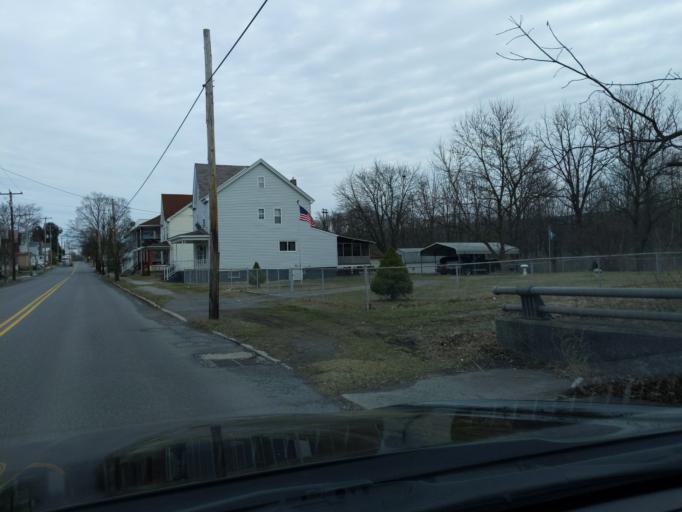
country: US
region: Pennsylvania
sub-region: Blair County
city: Greenwood
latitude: 40.5454
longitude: -78.3756
